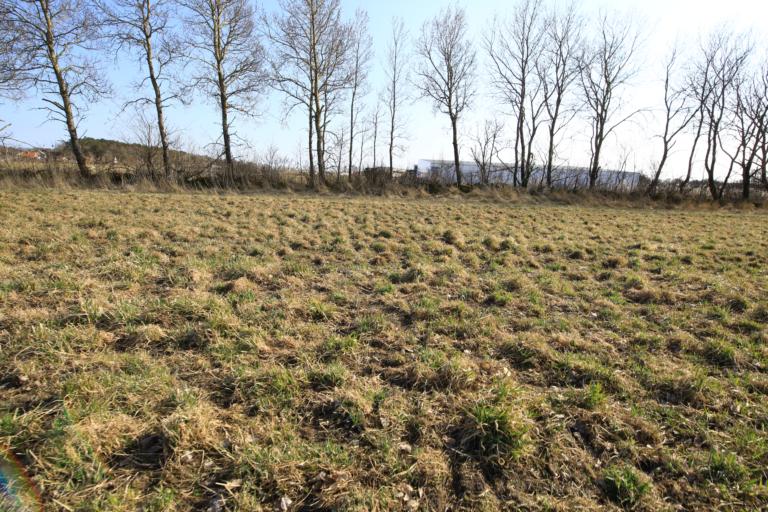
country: SE
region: Halland
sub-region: Varbergs Kommun
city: Varberg
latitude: 57.1401
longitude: 12.2762
